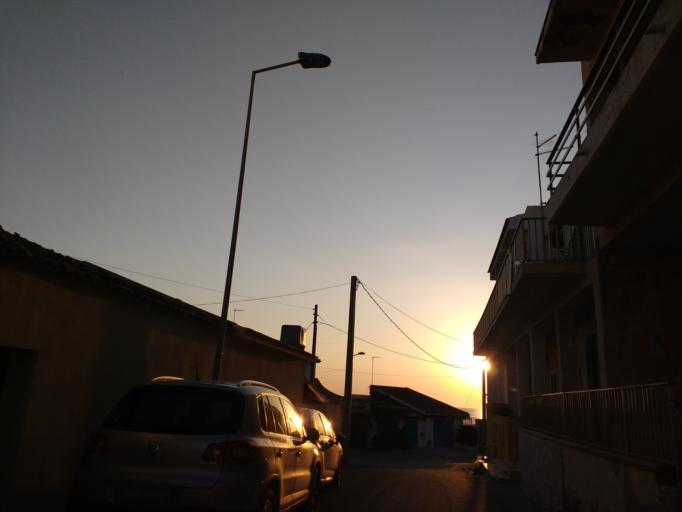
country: IT
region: Sicily
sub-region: Ragusa
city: Cava d'Aliga
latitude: 36.7307
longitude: 14.6829
